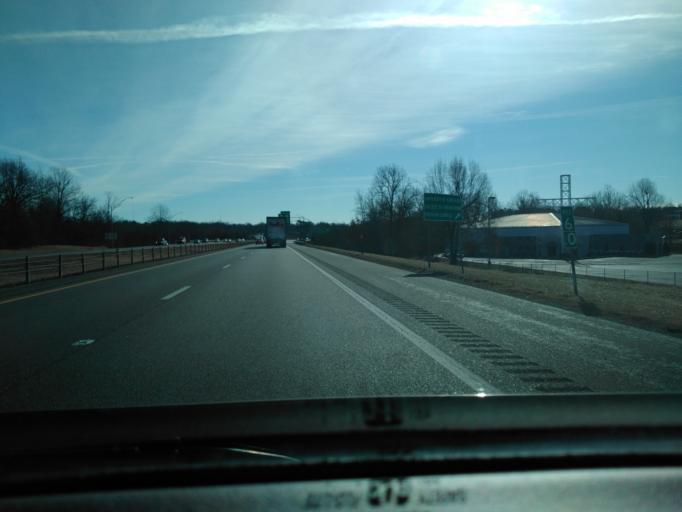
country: US
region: Kentucky
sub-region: McCracken County
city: Hendron
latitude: 37.0610
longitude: -88.6607
